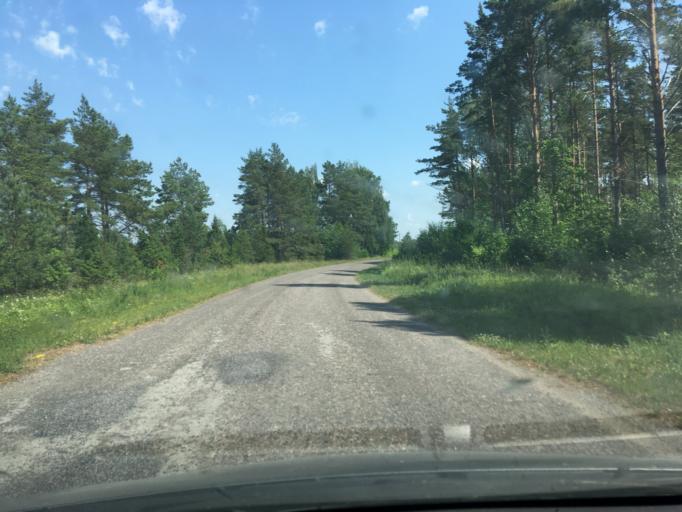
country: EE
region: Laeaene
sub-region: Lihula vald
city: Lihula
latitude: 58.6648
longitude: 23.7424
